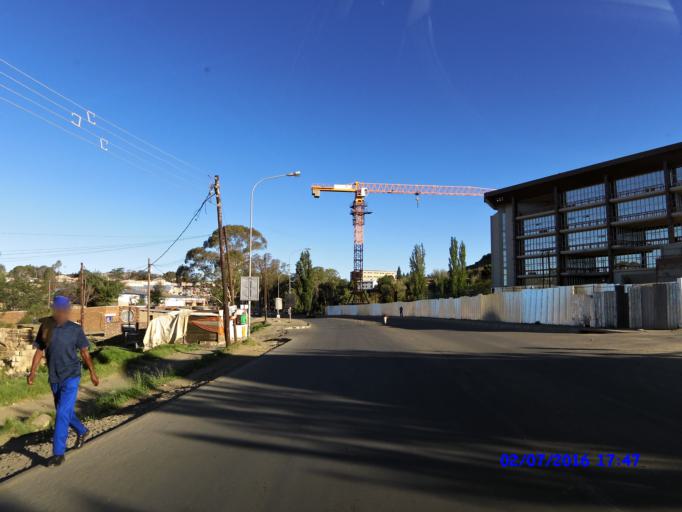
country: LS
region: Maseru
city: Maseru
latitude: -29.3118
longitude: 27.4890
